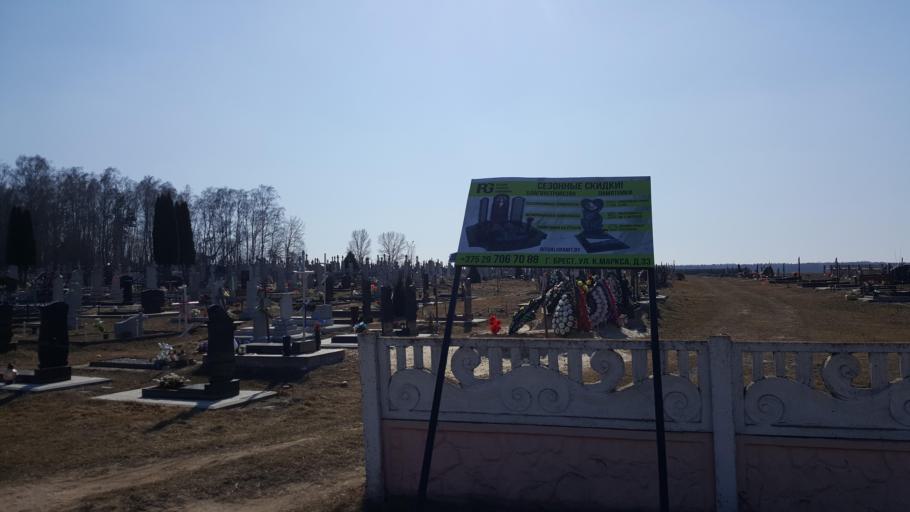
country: BY
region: Brest
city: Kamyanyets
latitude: 52.3586
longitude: 23.7742
